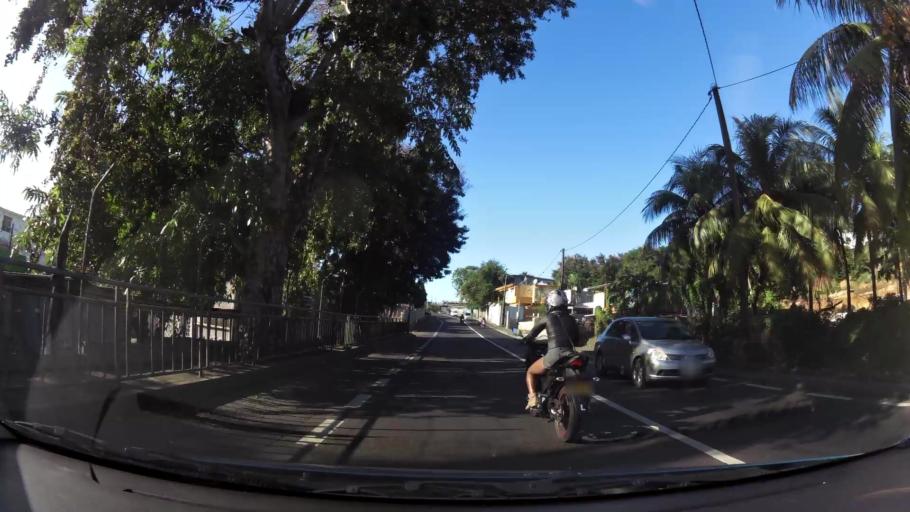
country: MU
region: Moka
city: Pailles
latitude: -20.1722
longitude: 57.4769
